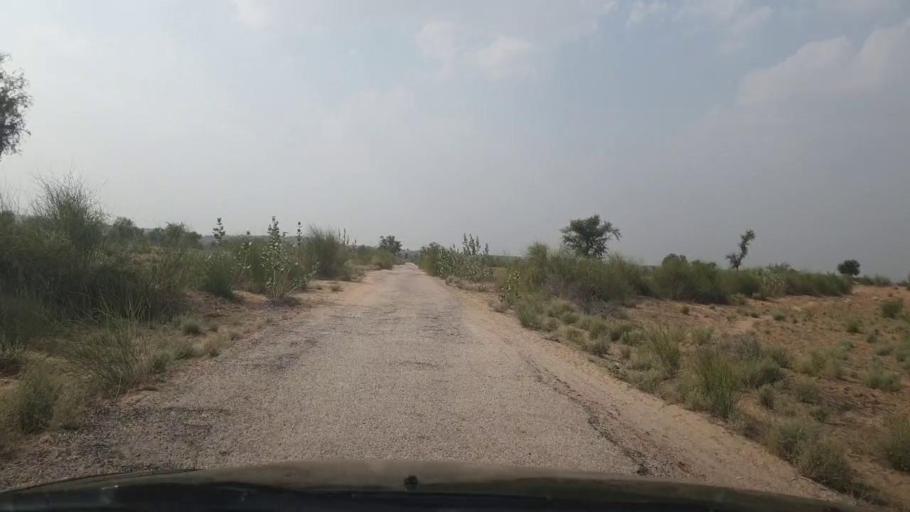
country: PK
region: Sindh
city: Islamkot
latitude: 24.9636
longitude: 70.6273
